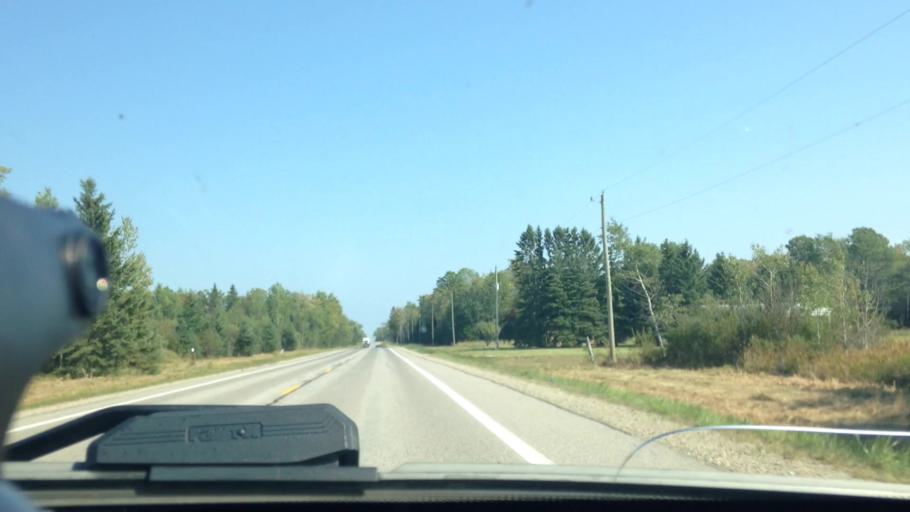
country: US
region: Michigan
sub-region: Luce County
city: Newberry
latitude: 46.3034
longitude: -85.3746
